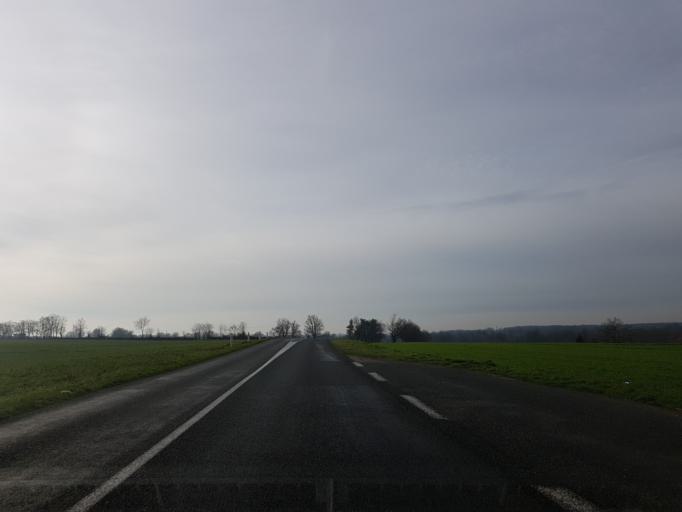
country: FR
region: Auvergne
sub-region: Departement de l'Allier
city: Lusigny
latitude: 46.6038
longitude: 3.5348
